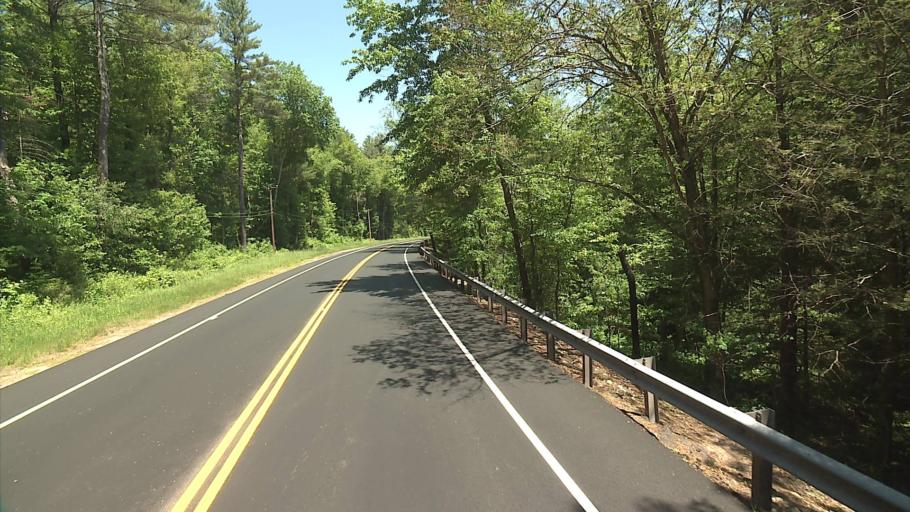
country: US
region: Connecticut
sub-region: Tolland County
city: Crystal Lake
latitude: 41.9626
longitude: -72.3649
